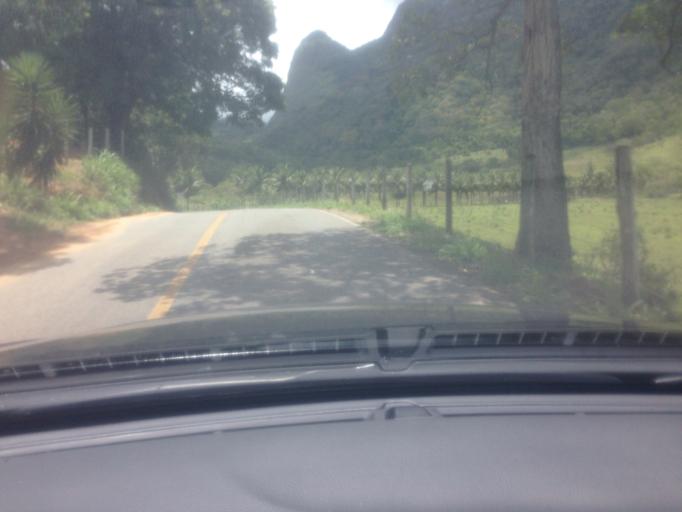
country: BR
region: Espirito Santo
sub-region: Guarapari
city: Guarapari
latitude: -20.6198
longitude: -40.5287
